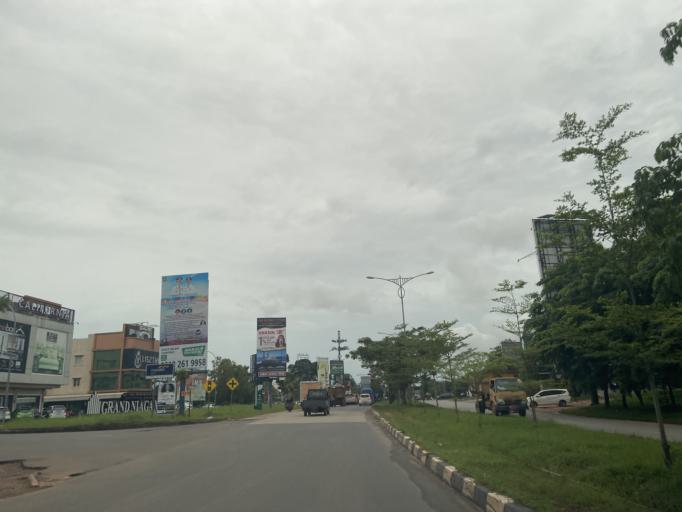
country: SG
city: Singapore
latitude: 1.1169
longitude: 104.0585
